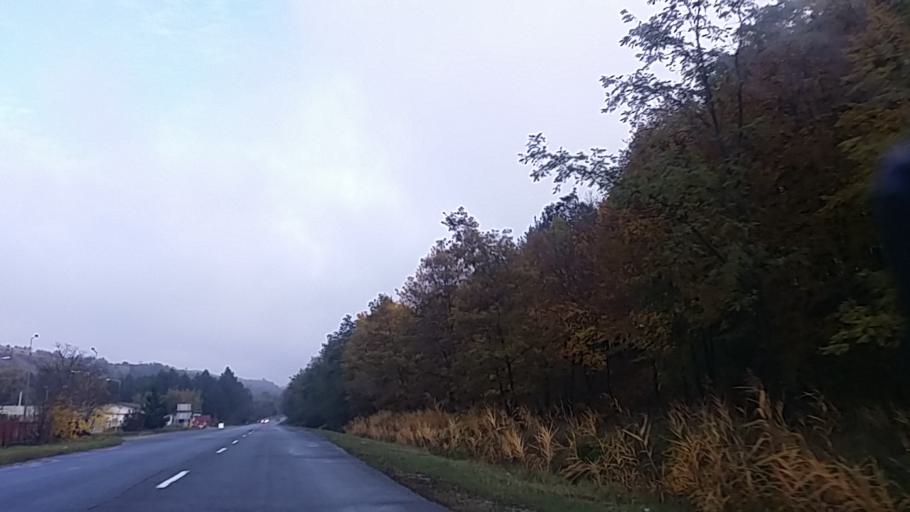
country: HU
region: Heves
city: Belapatfalva
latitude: 48.0708
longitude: 20.3575
